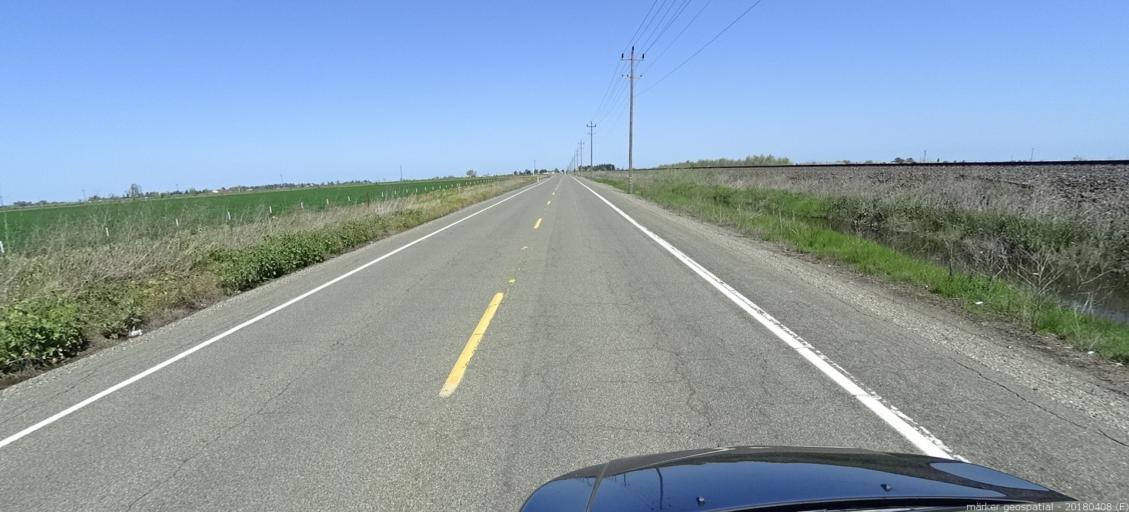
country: US
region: California
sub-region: San Joaquin County
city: Thornton
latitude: 38.3086
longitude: -121.4432
